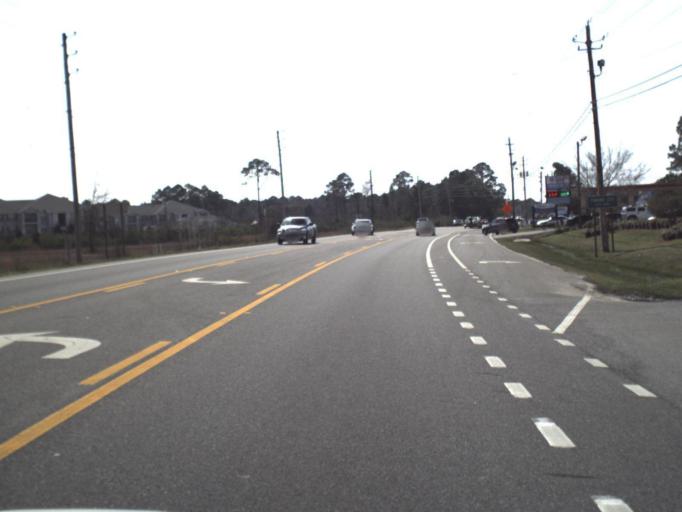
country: US
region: Florida
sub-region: Bay County
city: Lynn Haven
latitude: 30.2206
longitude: -85.6641
